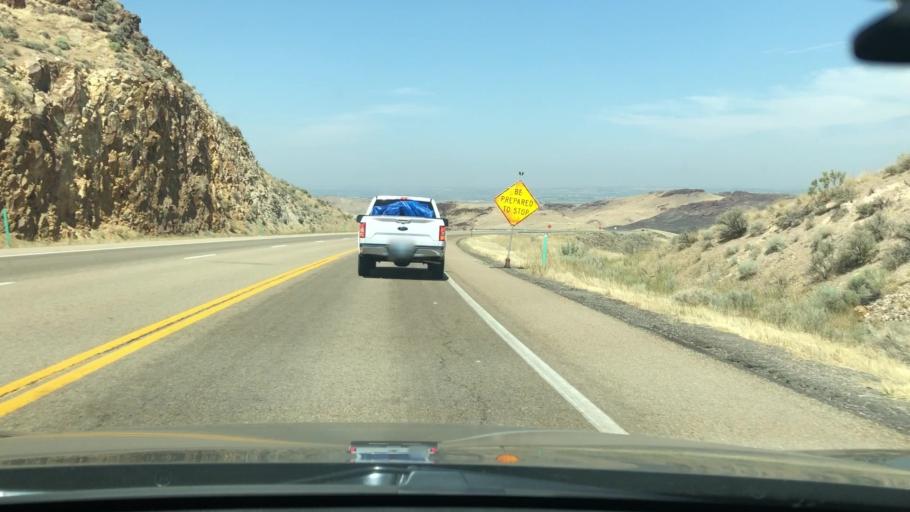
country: US
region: Idaho
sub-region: Owyhee County
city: Marsing
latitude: 43.4321
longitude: -116.8608
